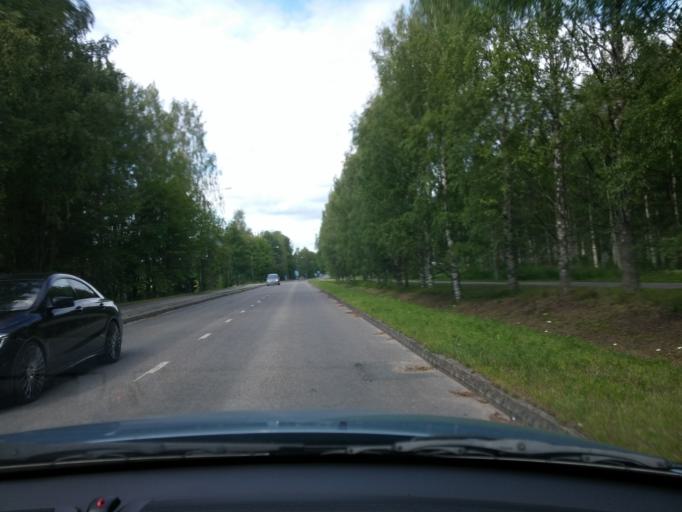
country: FI
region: Central Finland
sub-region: Saarijaervi-Viitasaari
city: Saarijaervi
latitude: 62.7068
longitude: 25.2295
